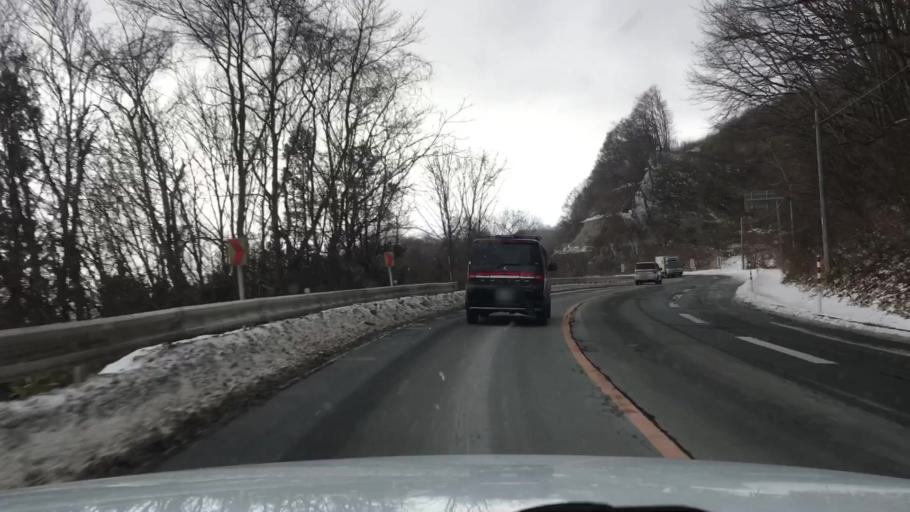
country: JP
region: Iwate
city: Morioka-shi
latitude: 39.6565
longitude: 141.3407
